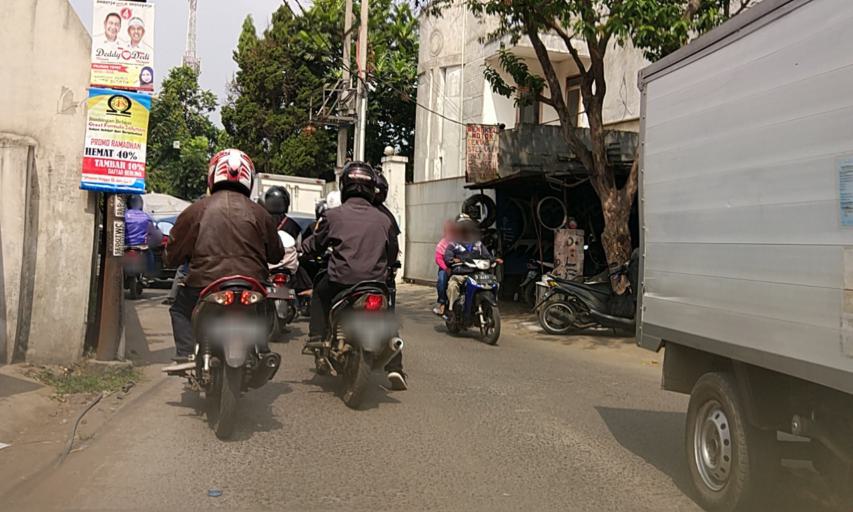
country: ID
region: West Java
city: Margahayukencana
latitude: -6.9369
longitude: 107.5832
